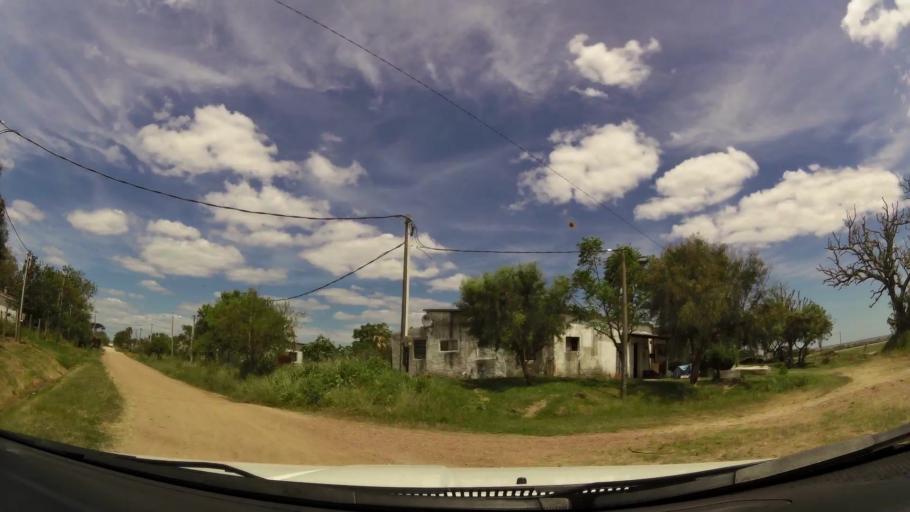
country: UY
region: San Jose
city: Delta del Tigre
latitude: -34.7529
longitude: -56.4253
